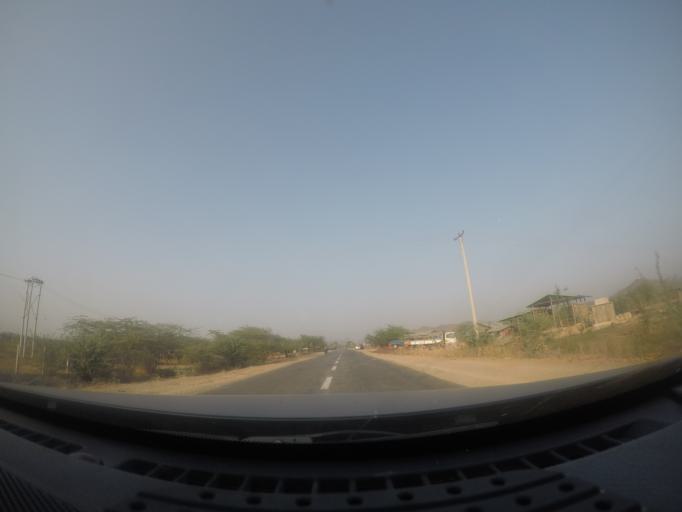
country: MM
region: Mandalay
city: Yamethin
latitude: 20.7002
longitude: 96.1707
